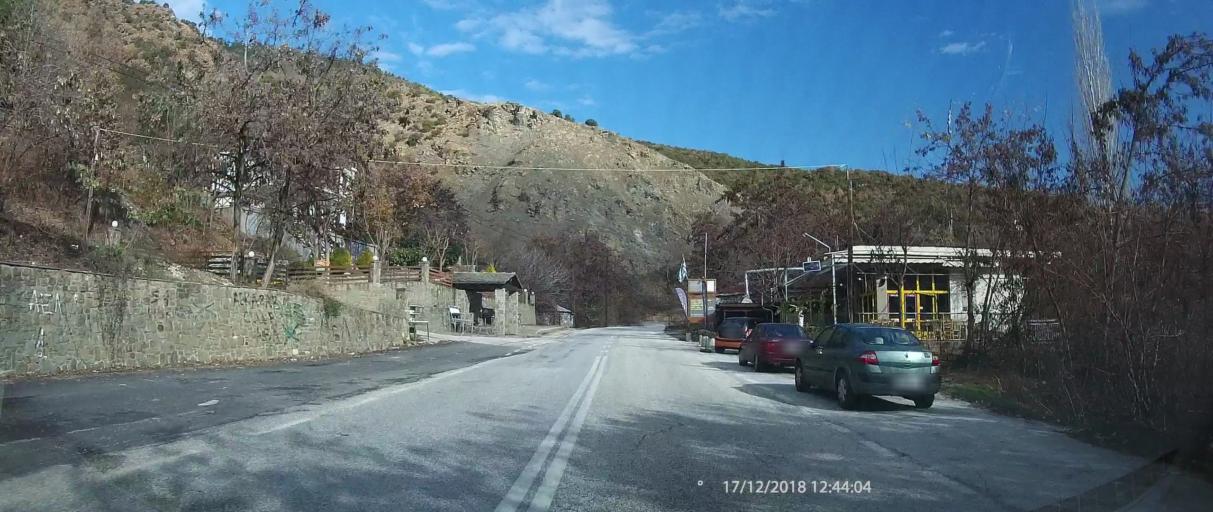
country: GR
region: Epirus
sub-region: Nomos Ioanninon
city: Metsovo
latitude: 39.7848
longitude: 21.3970
